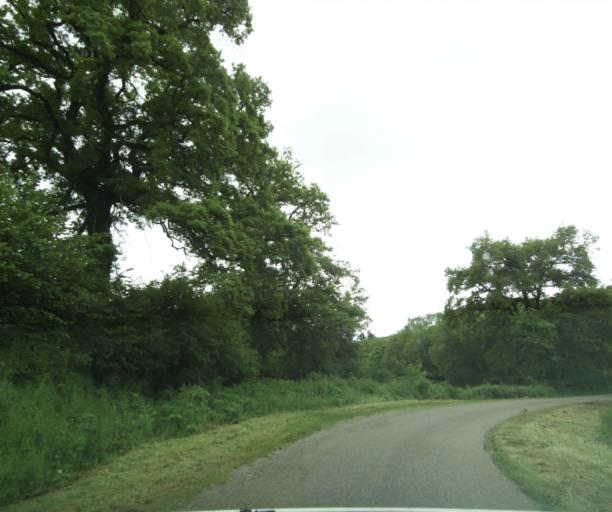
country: FR
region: Bourgogne
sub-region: Departement de Saone-et-Loire
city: Charolles
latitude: 46.4660
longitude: 4.2906
